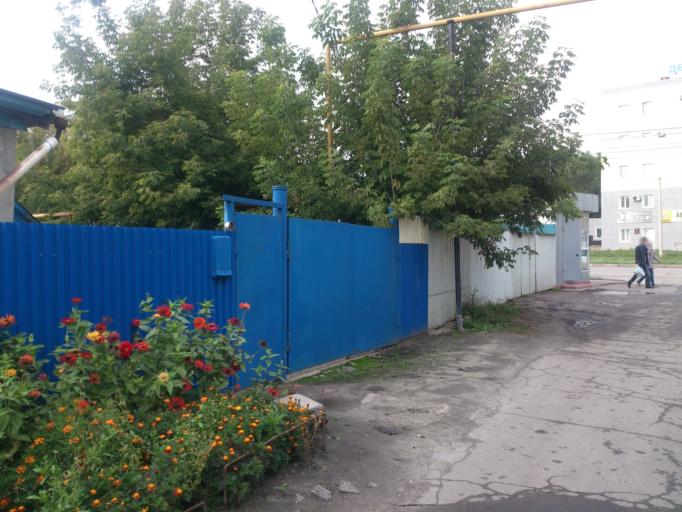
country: RU
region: Ulyanovsk
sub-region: Ulyanovskiy Rayon
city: Ulyanovsk
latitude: 54.2821
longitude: 48.3081
